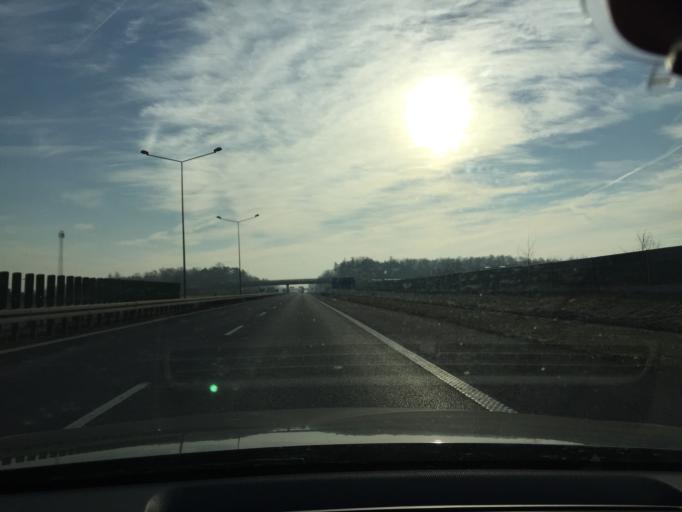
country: PL
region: Silesian Voivodeship
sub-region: Powiat gliwicki
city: Sosnicowice
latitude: 50.3415
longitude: 18.5433
